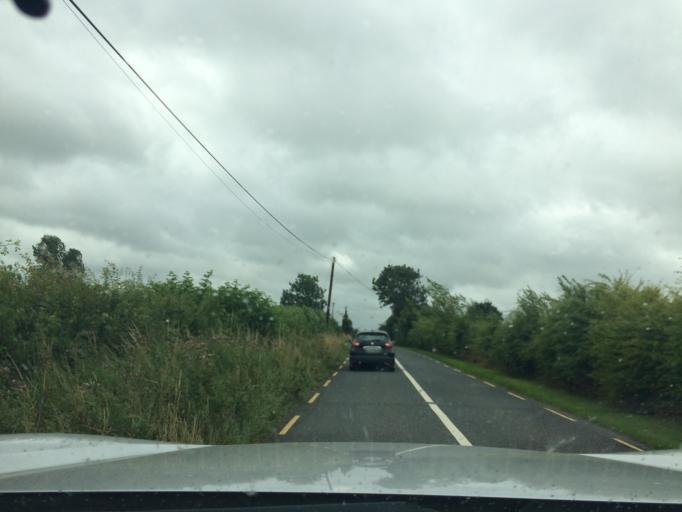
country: IE
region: Munster
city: Thurles
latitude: 52.6174
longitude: -7.8805
